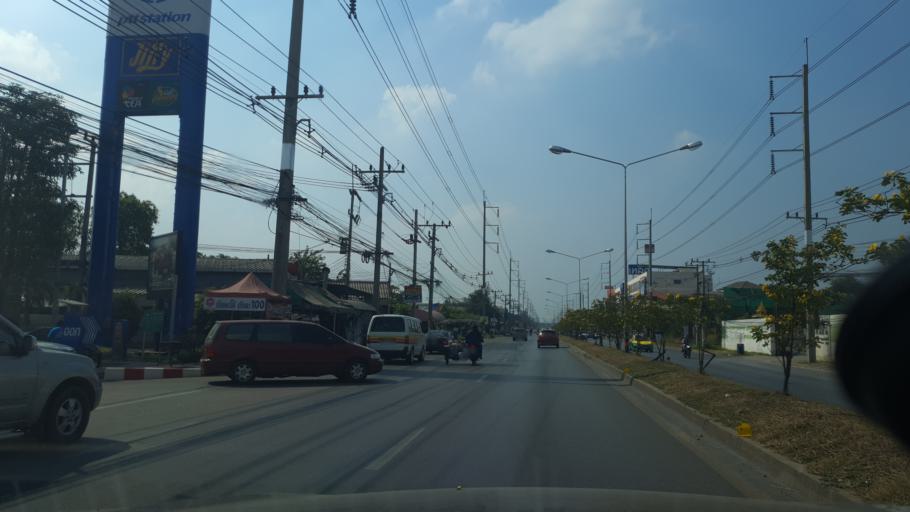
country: TH
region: Samut Sakhon
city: Krathum Baen
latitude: 13.6714
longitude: 100.2815
